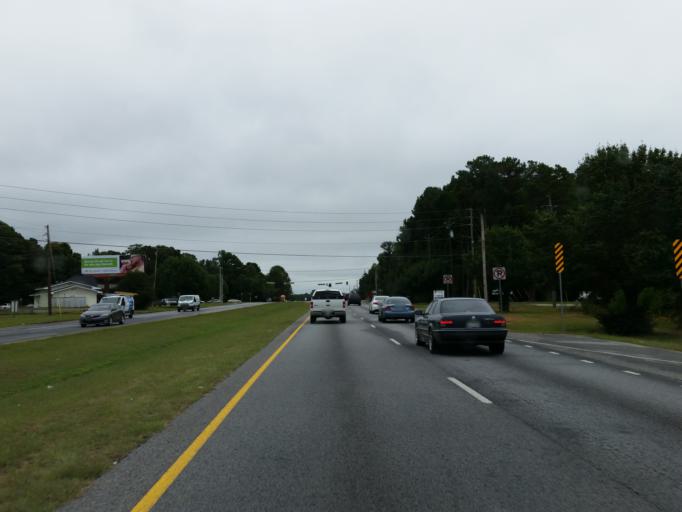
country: US
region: Georgia
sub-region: Clayton County
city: Bonanza
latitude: 33.4835
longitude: -84.3397
